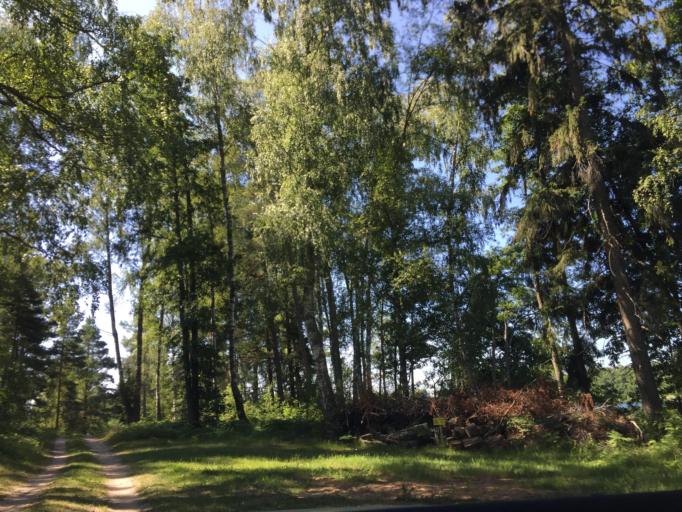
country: LV
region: Talsu Rajons
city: Stende
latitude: 57.1583
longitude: 22.3036
